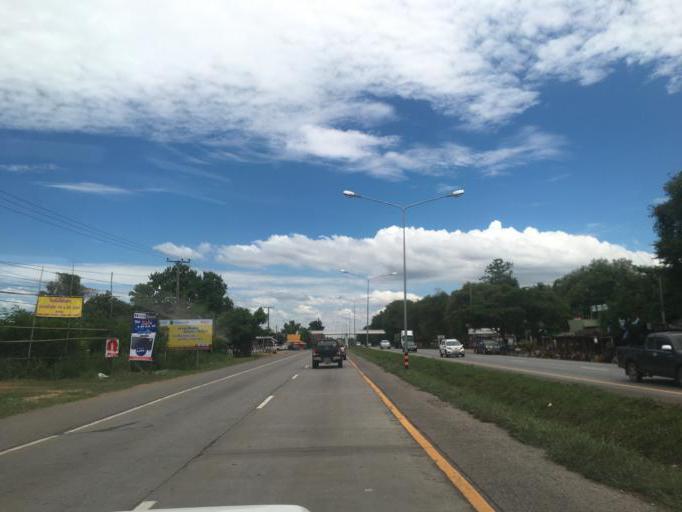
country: TH
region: Khon Kaen
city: Nam Phong
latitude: 16.6335
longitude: 102.7996
